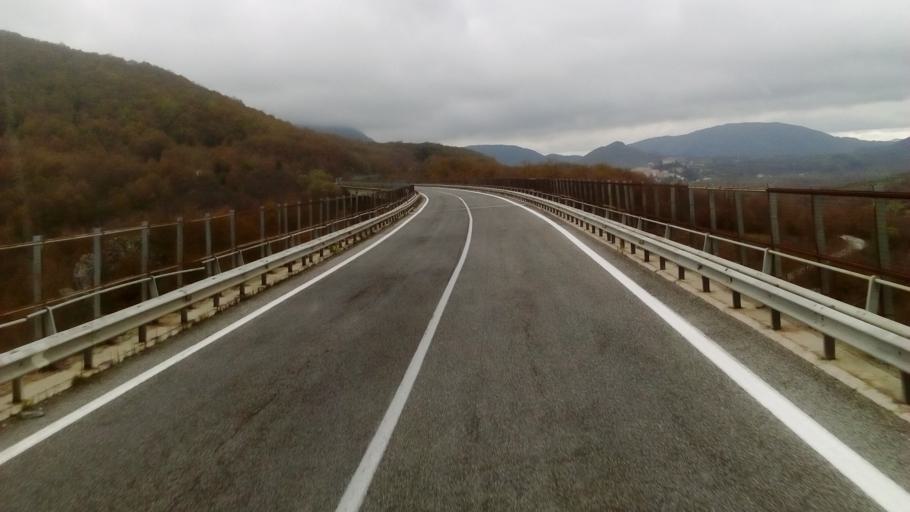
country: IT
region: Molise
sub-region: Provincia di Isernia
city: Chiauci
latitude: 41.6725
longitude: 14.3709
